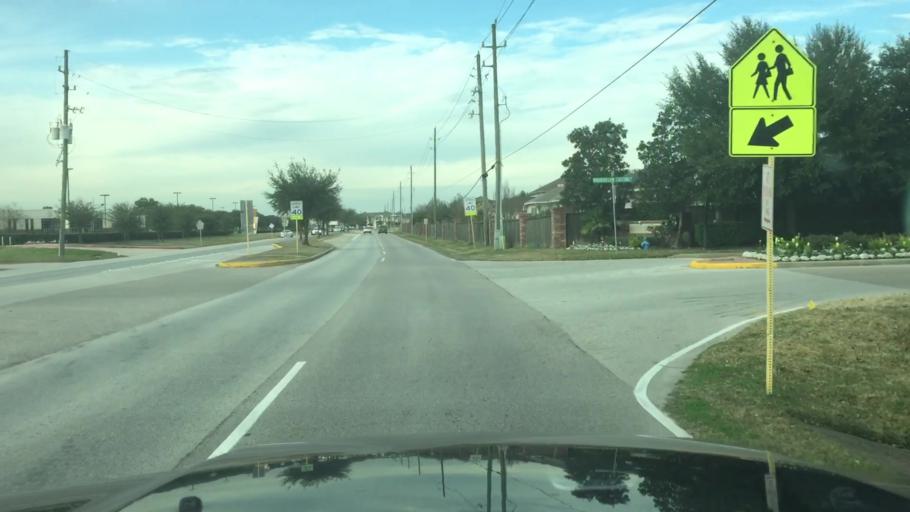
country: US
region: Texas
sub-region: Harris County
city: Oak Cliff Place
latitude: 29.8545
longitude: -95.6683
